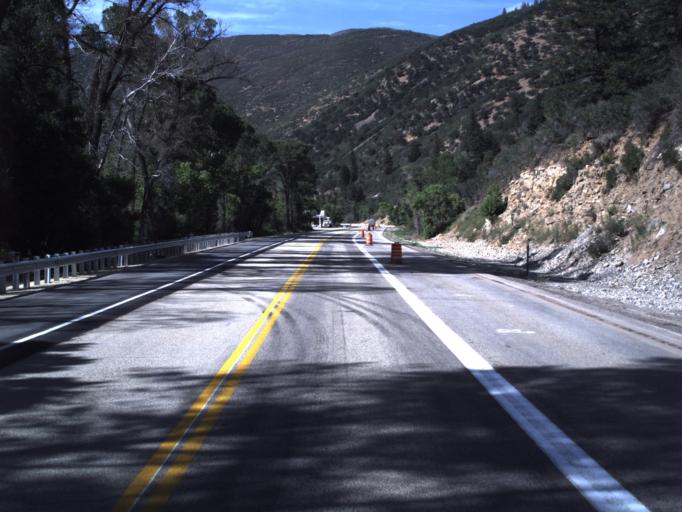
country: US
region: Utah
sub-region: Wasatch County
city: Heber
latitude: 40.3899
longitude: -111.3030
